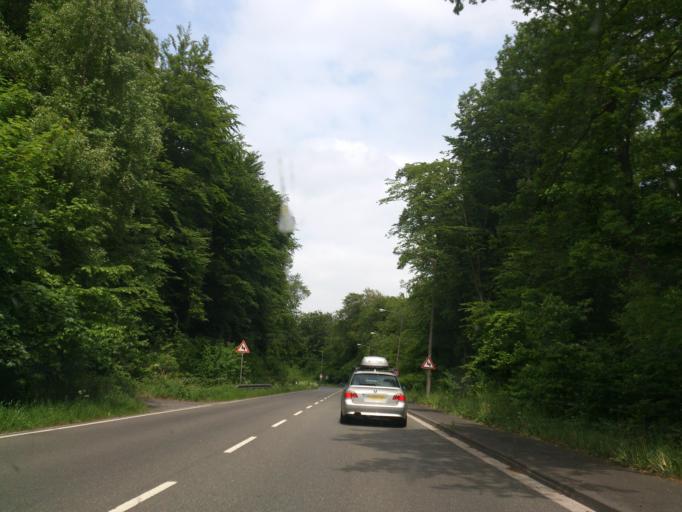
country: DE
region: Hesse
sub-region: Regierungsbezirk Kassel
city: Baunatal
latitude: 51.2818
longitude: 9.4068
